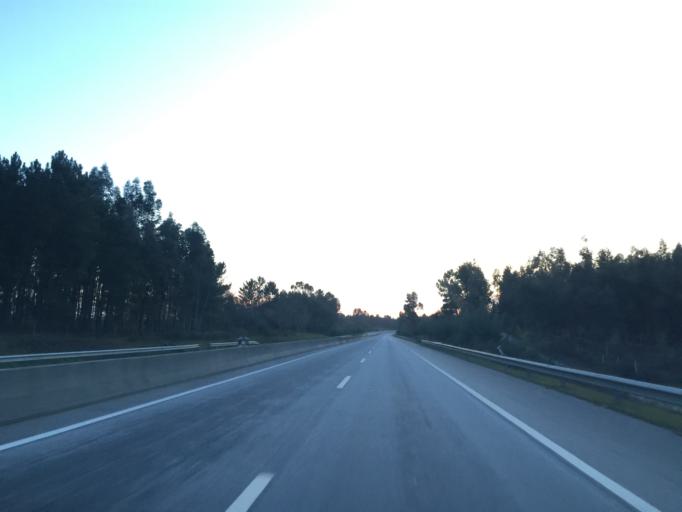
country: PT
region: Viseu
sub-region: Santa Comba Dao
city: Santa Comba Dao
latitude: 40.4049
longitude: -8.0746
